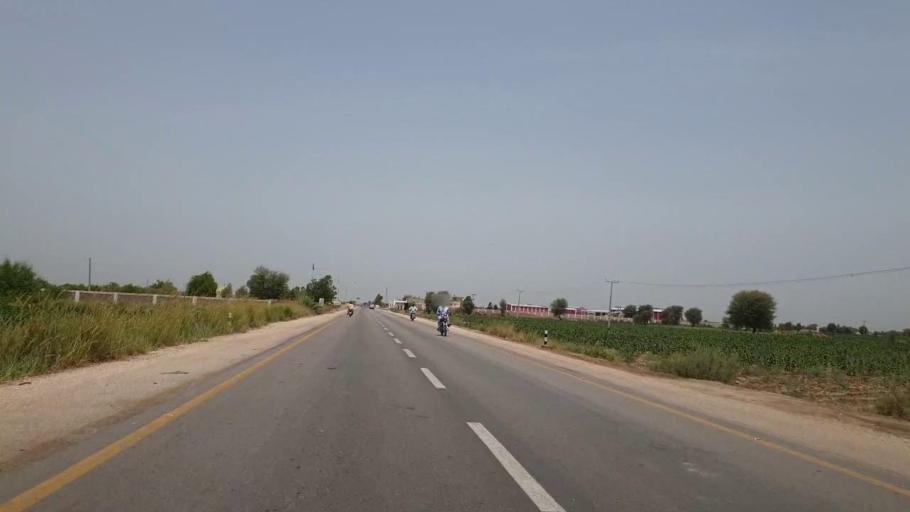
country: PK
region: Sindh
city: Shahpur Chakar
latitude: 26.1943
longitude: 68.5701
